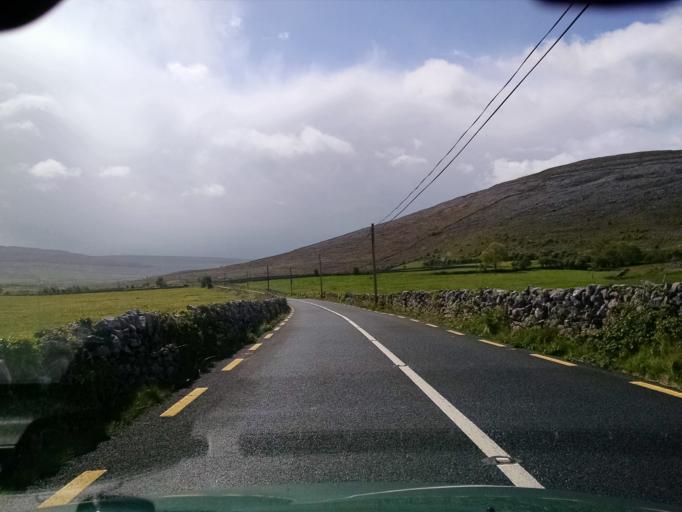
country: IE
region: Connaught
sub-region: County Galway
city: Bearna
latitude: 53.1316
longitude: -9.0966
